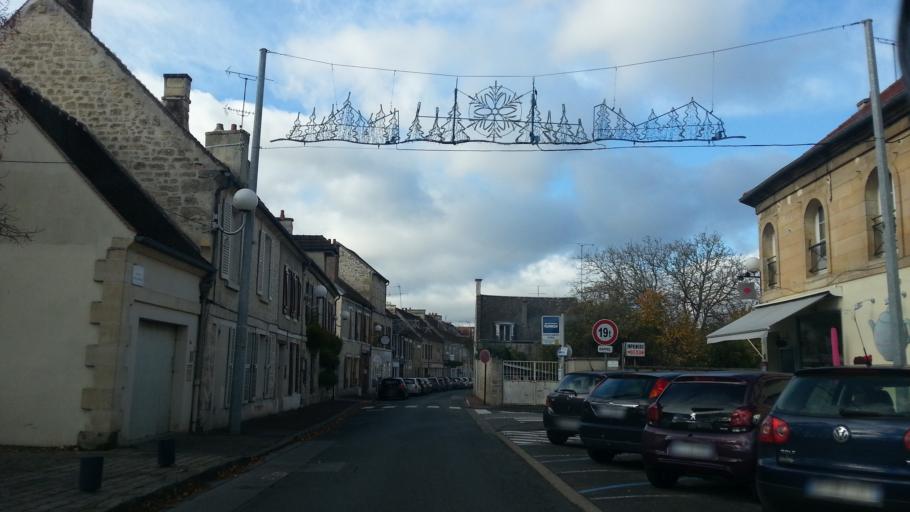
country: FR
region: Picardie
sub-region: Departement de l'Oise
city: Gouvieux
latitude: 49.1879
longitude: 2.4194
